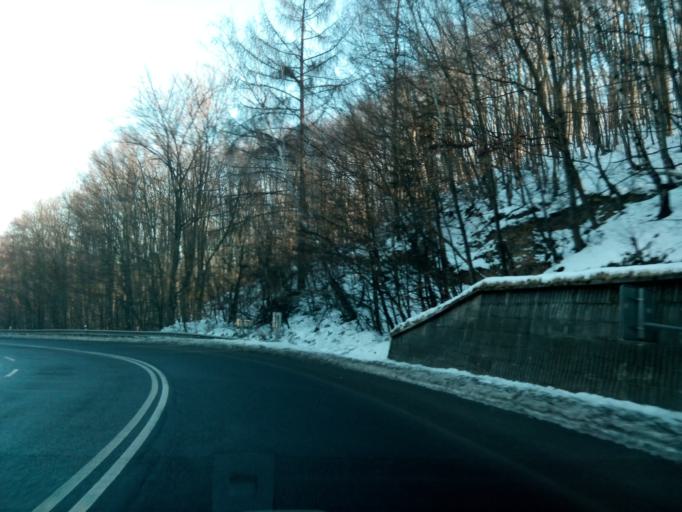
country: SK
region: Kosicky
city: Secovce
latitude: 48.7333
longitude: 21.5390
